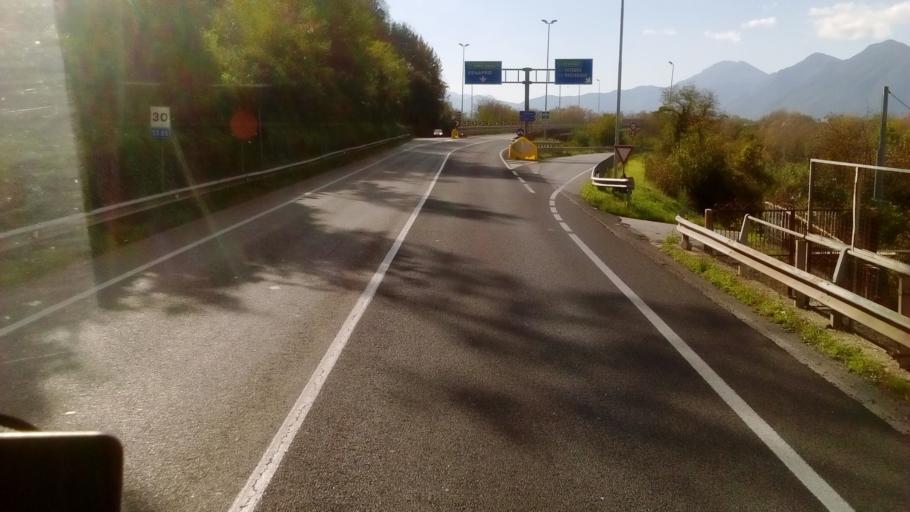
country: IT
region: Molise
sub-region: Provincia di Isernia
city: Taverna Ravindola
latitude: 41.5198
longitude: 14.1430
